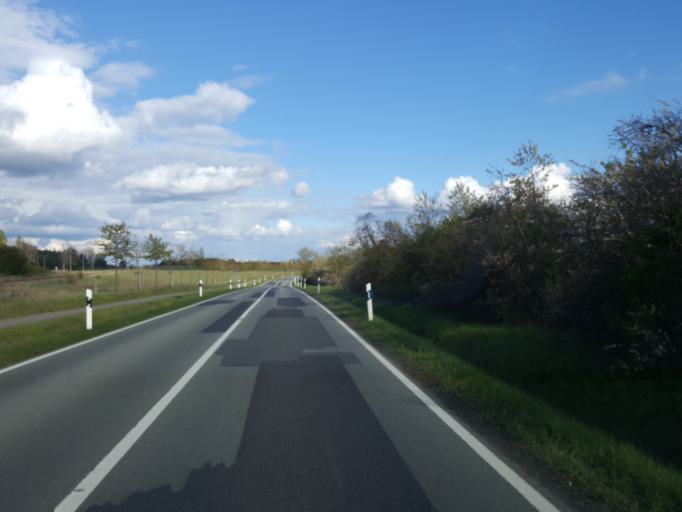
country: DE
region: Mecklenburg-Vorpommern
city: Grabowhofe
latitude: 53.5331
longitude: 12.6239
